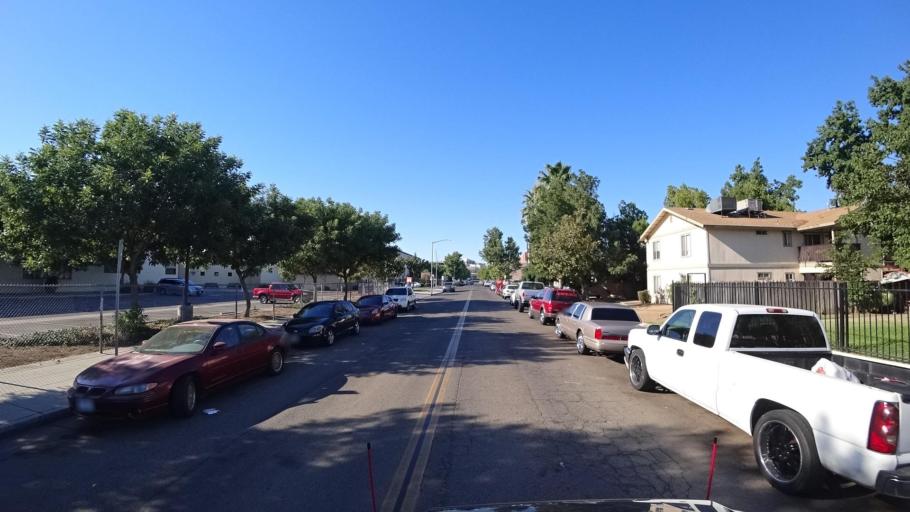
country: US
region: California
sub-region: Fresno County
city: Fresno
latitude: 36.7478
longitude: -119.7838
